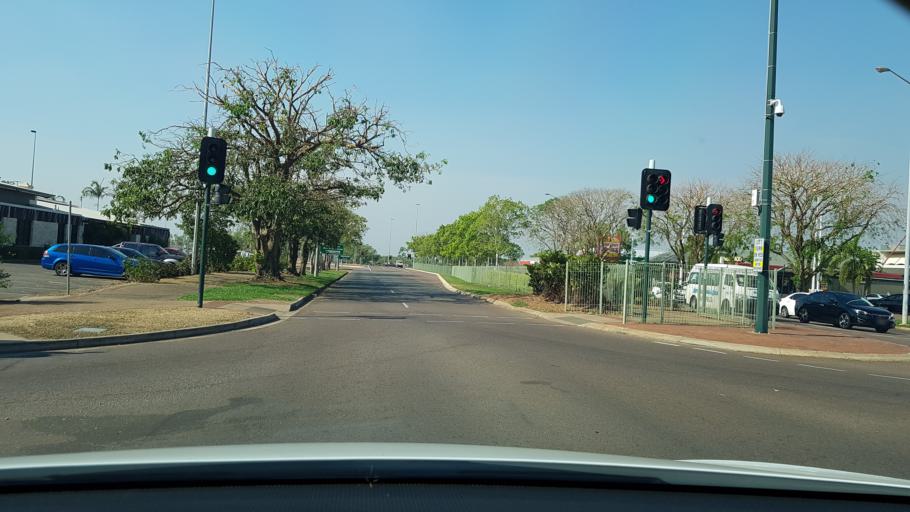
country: AU
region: Northern Territory
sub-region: Palmerston
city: Palmerston
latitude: -12.4807
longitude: 130.9867
